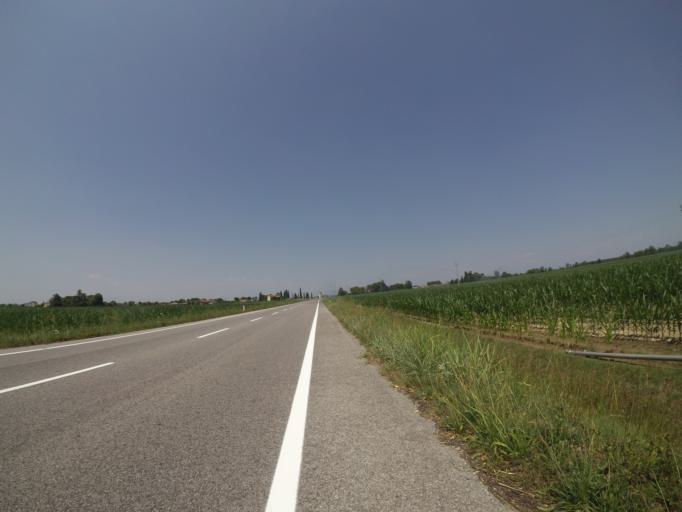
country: IT
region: Friuli Venezia Giulia
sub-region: Provincia di Udine
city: Varmo
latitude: 45.9018
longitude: 13.0054
